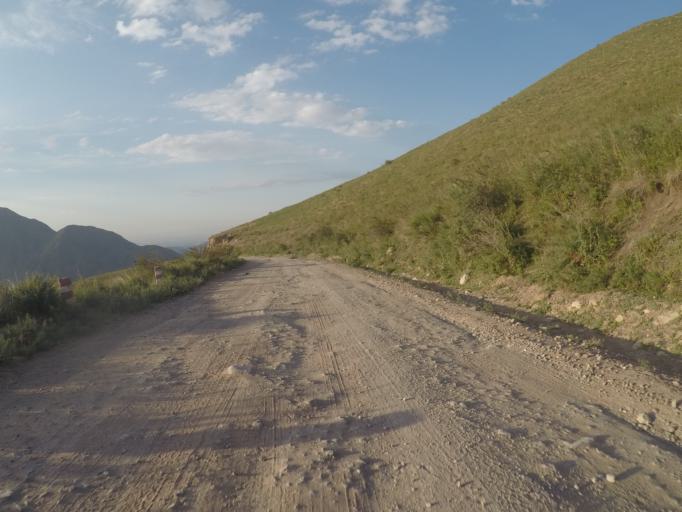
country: KG
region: Chuy
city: Bishkek
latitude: 42.6546
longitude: 74.6629
